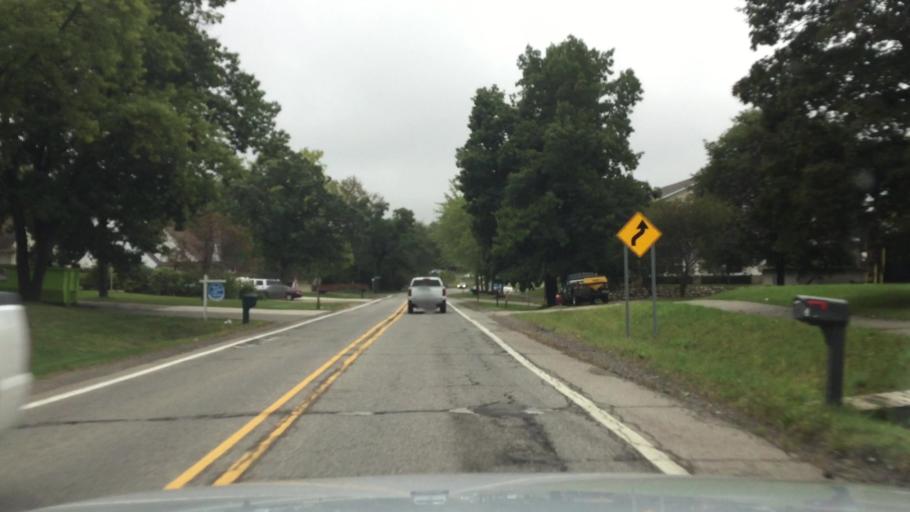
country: US
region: Michigan
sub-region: Oakland County
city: Waterford
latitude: 42.6879
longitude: -83.4088
